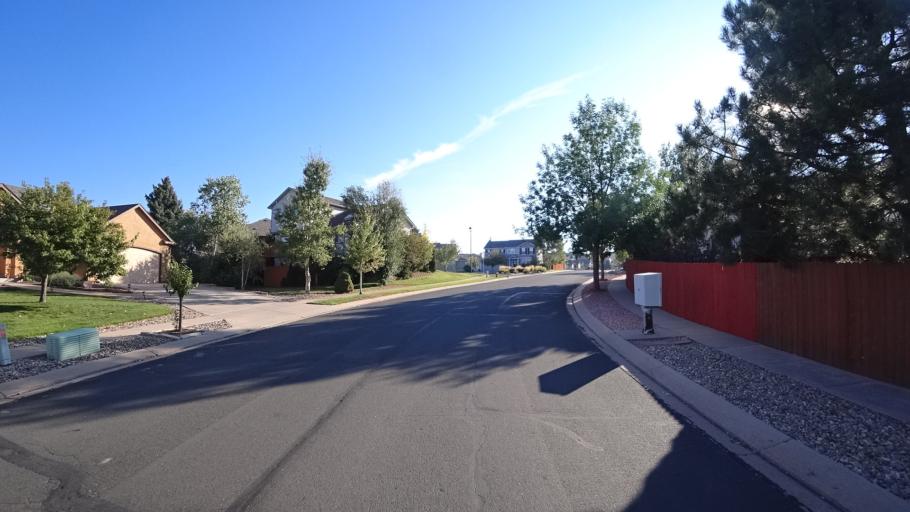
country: US
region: Colorado
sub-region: El Paso County
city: Cimarron Hills
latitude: 38.8926
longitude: -104.7035
